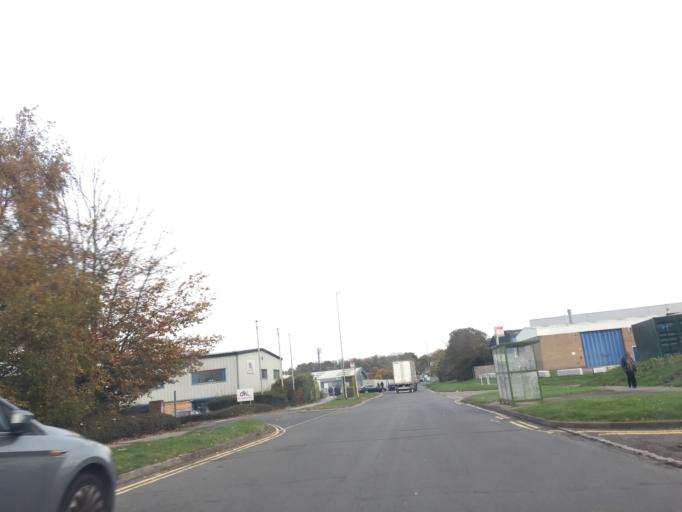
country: GB
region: England
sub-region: Northamptonshire
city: Northampton
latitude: 52.2758
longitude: -0.8708
